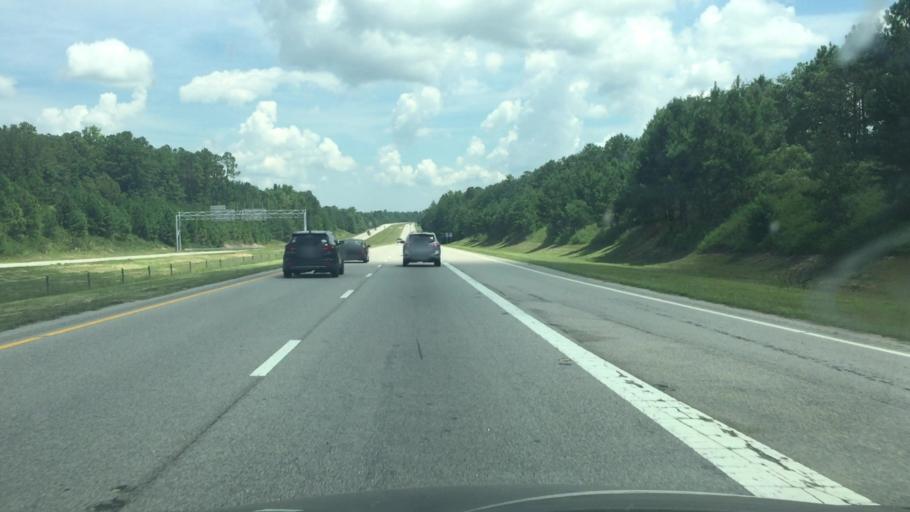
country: US
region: North Carolina
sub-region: Richmond County
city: Ellerbe
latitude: 35.0460
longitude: -79.7654
